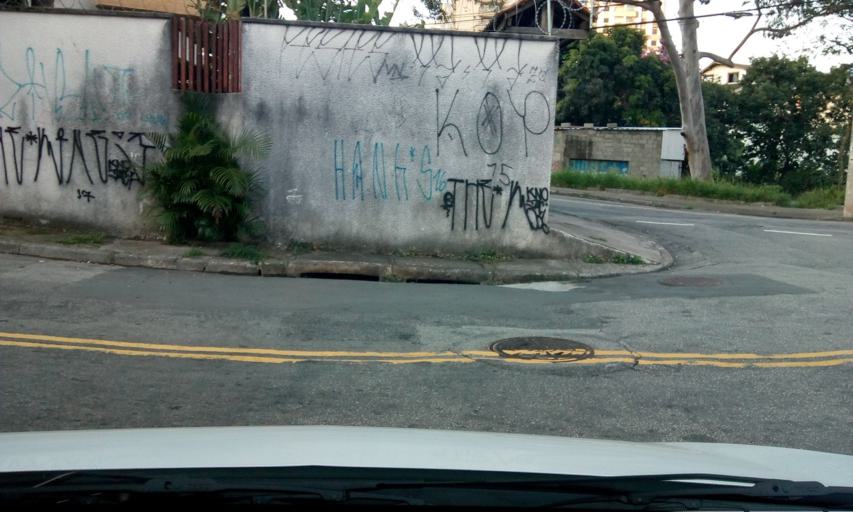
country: BR
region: Sao Paulo
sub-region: Sao Paulo
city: Sao Paulo
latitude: -23.4867
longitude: -46.6127
